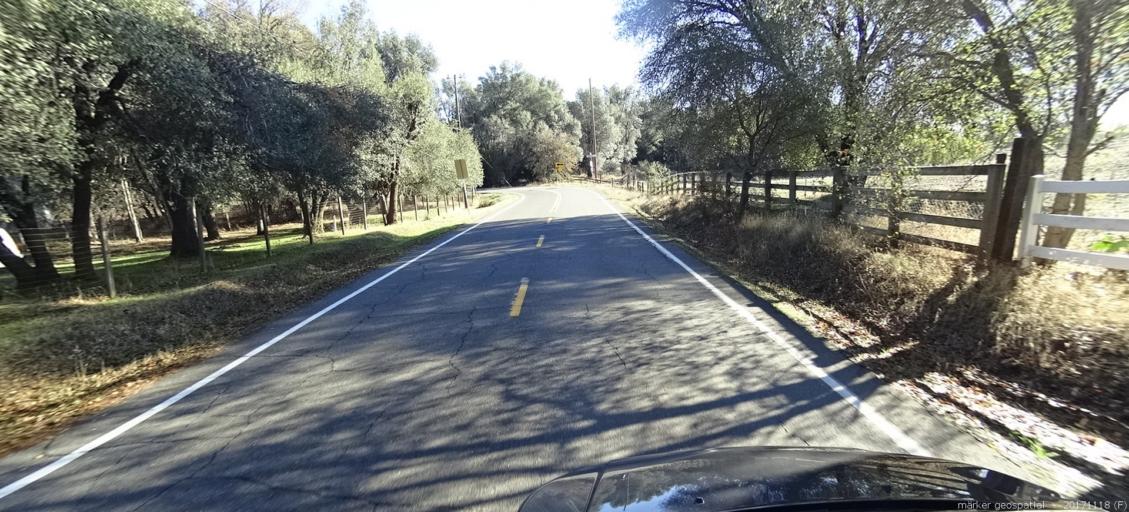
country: US
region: California
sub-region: Shasta County
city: Cottonwood
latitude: 40.3819
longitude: -122.3221
